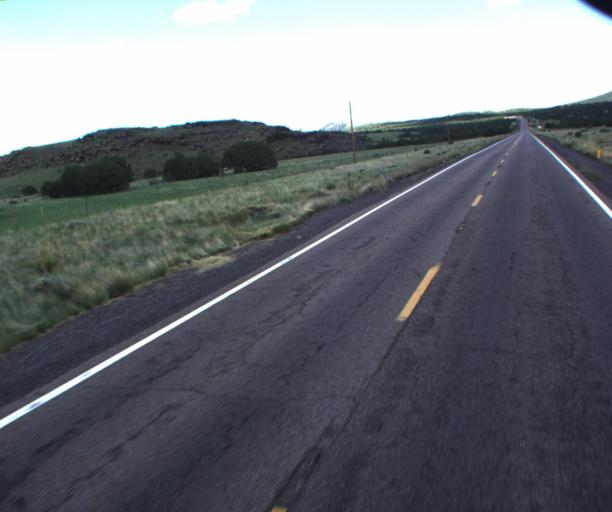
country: US
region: Arizona
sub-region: Navajo County
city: Pinetop-Lakeside
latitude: 34.2692
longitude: -109.6301
